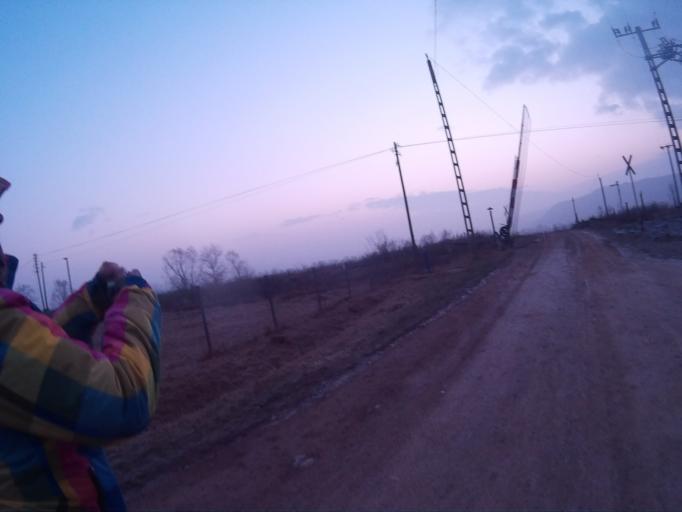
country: HU
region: Borsod-Abauj-Zemplen
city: Szendro
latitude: 48.5352
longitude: 20.7354
